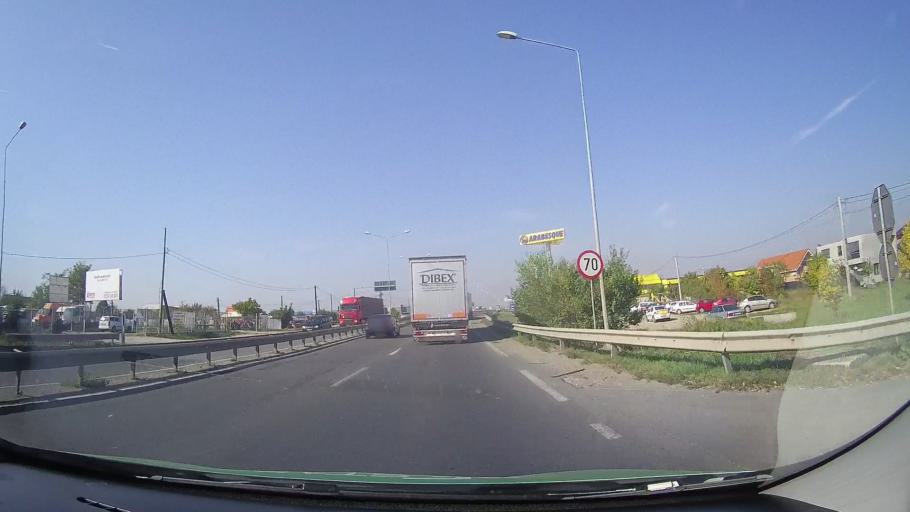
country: RO
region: Bihor
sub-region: Comuna Biharea
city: Oradea
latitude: 47.0471
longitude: 21.8978
